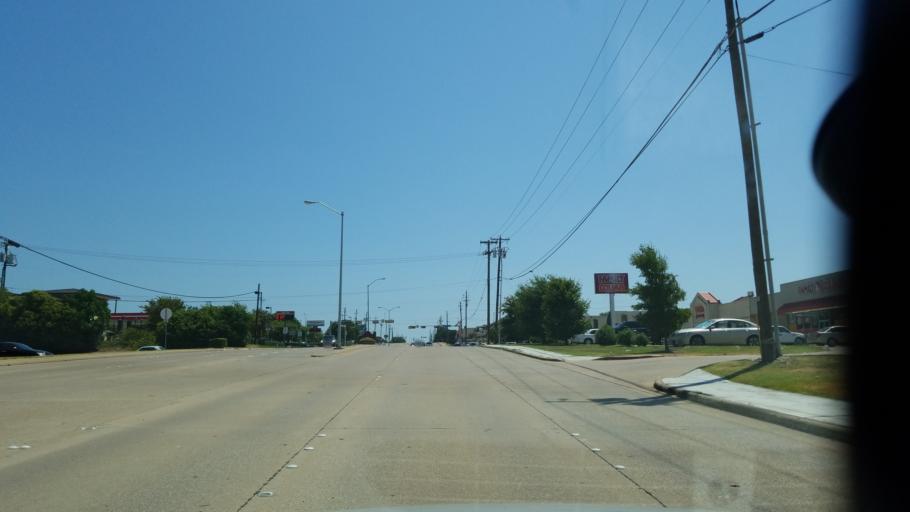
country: US
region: Texas
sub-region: Dallas County
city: Duncanville
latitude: 32.6474
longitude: -96.8933
